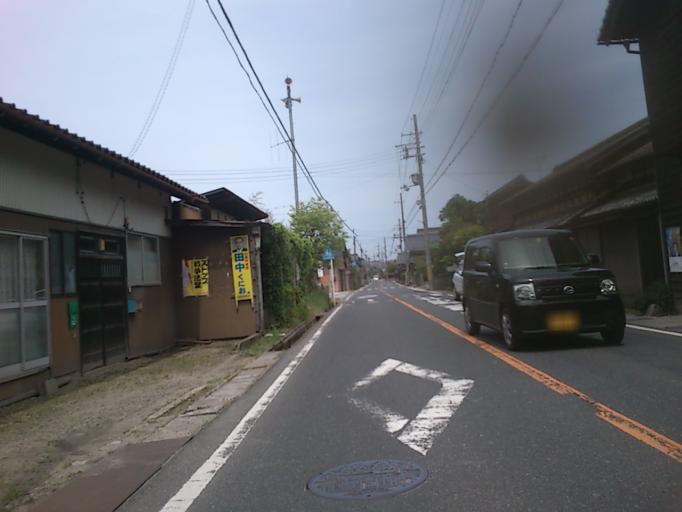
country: JP
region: Kyoto
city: Miyazu
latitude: 35.5990
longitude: 135.0936
